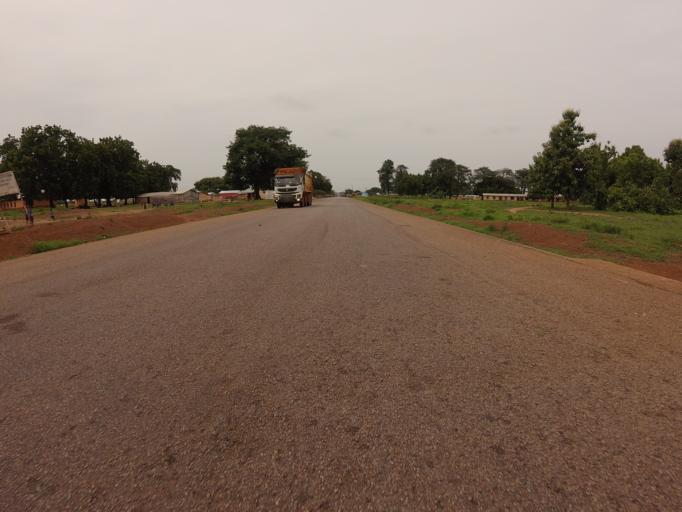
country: GH
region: Northern
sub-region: Yendi
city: Yendi
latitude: 9.3710
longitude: -0.0061
